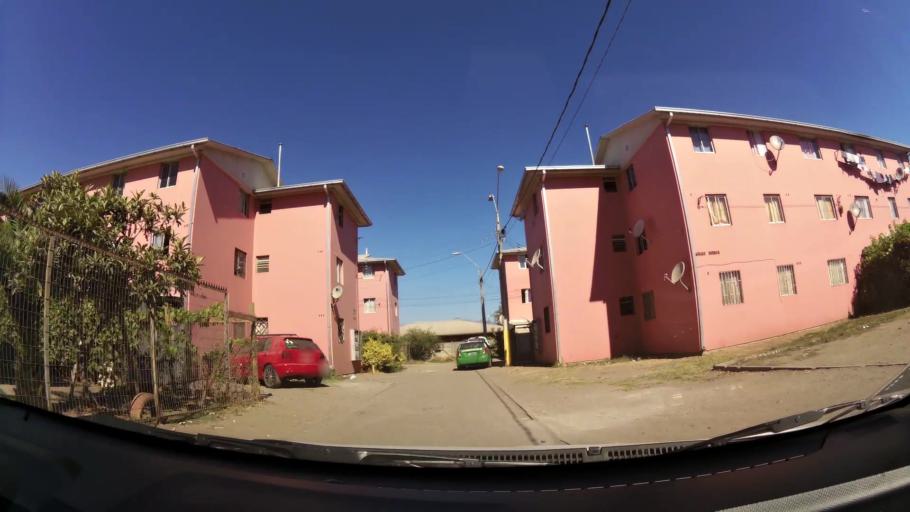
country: CL
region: O'Higgins
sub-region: Provincia de Colchagua
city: Chimbarongo
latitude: -34.5733
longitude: -71.0000
